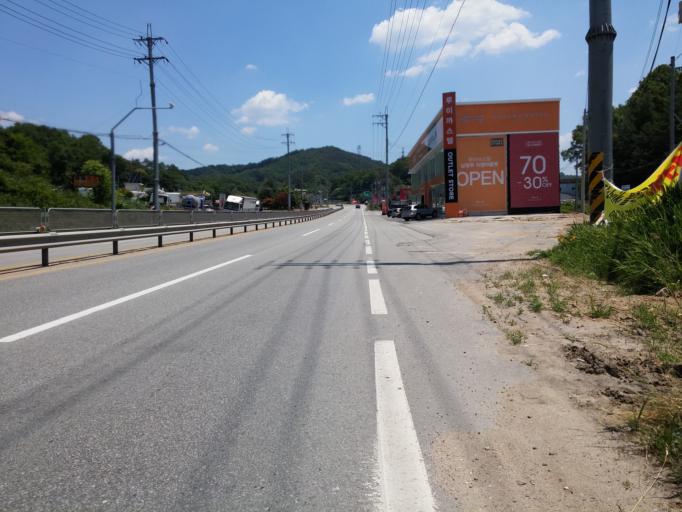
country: KR
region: Chungcheongbuk-do
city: Cheongju-si
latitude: 36.5625
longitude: 127.4428
